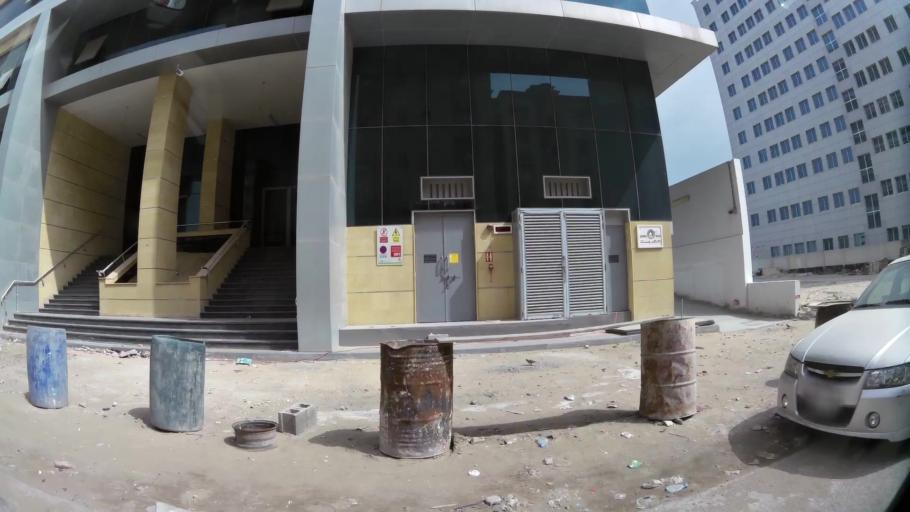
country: QA
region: Baladiyat ad Dawhah
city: Doha
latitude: 25.2900
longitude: 51.5052
